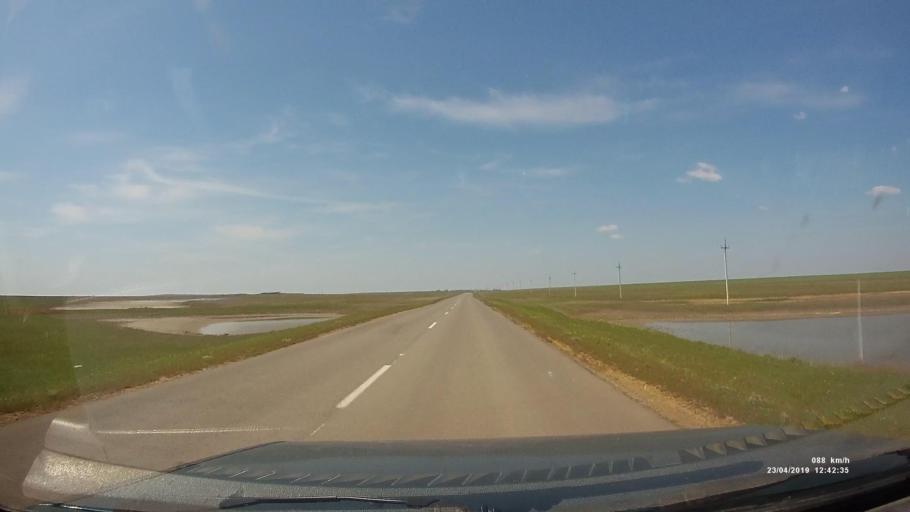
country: RU
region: Kalmykiya
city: Yashalta
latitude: 46.4570
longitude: 42.6634
